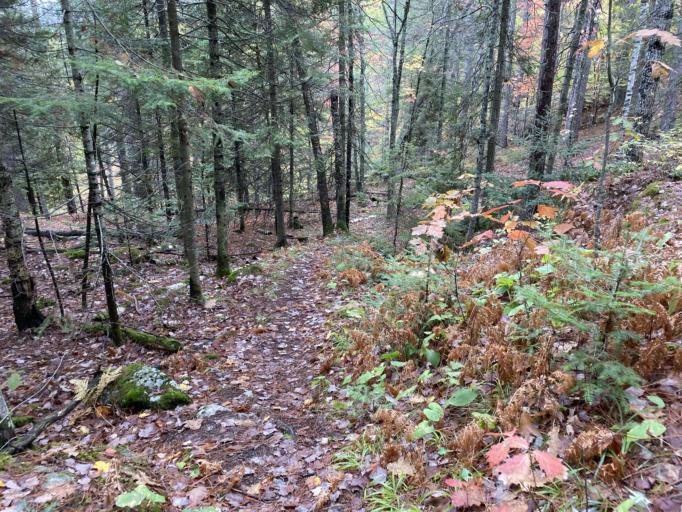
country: US
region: Michigan
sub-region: Marquette County
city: West Ishpeming
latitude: 46.5389
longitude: -87.9973
